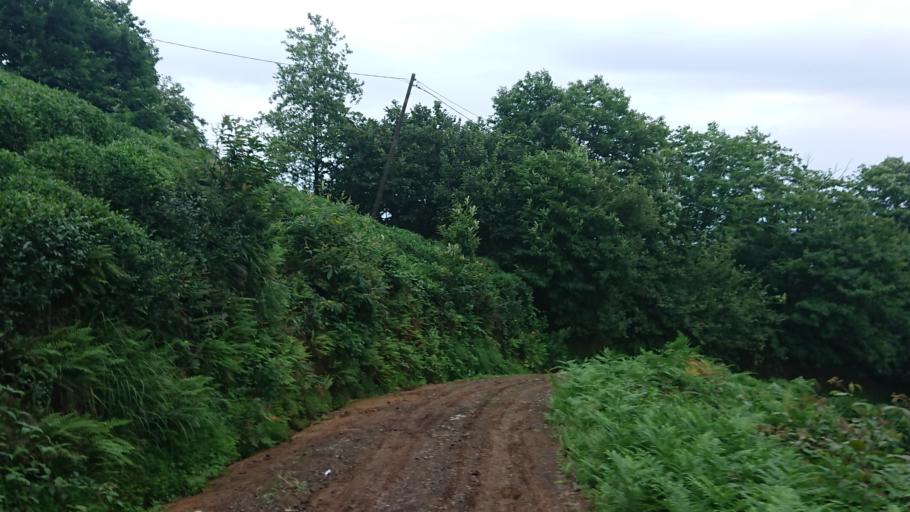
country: TR
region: Rize
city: Rize
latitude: 40.9891
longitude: 40.5071
